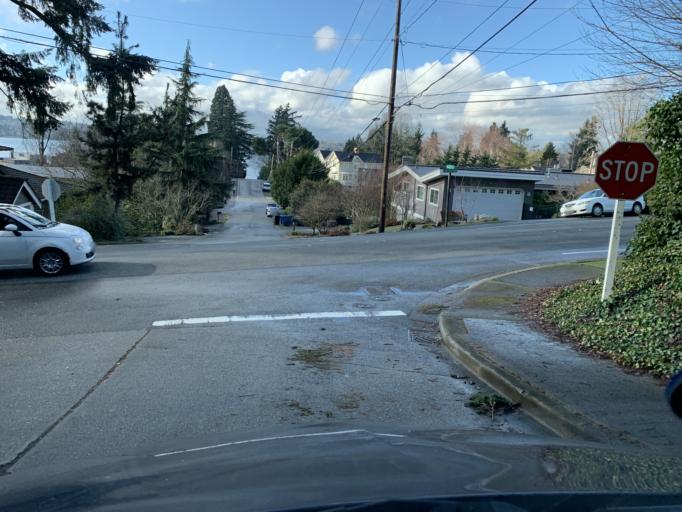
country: US
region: Washington
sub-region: King County
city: Mercer Island
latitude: 47.5819
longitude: -122.2484
